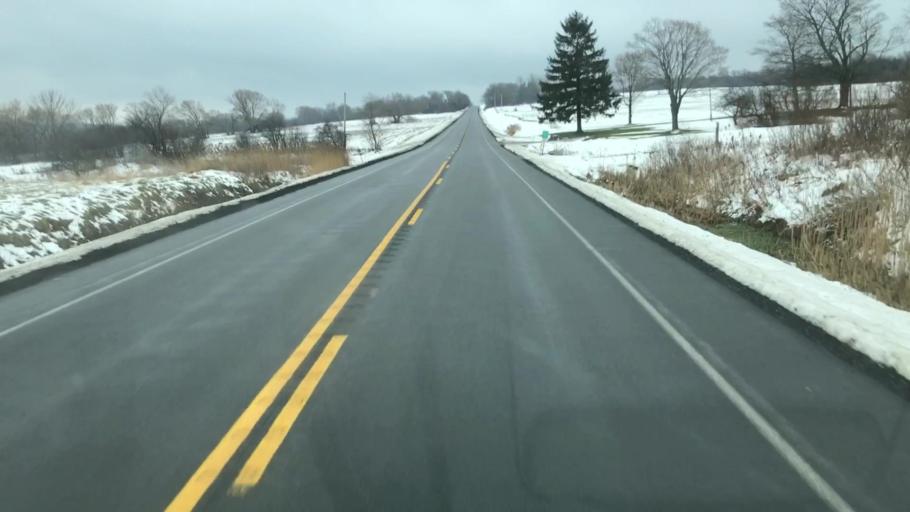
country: US
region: New York
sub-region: Cayuga County
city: Moravia
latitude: 42.7837
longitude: -76.3429
